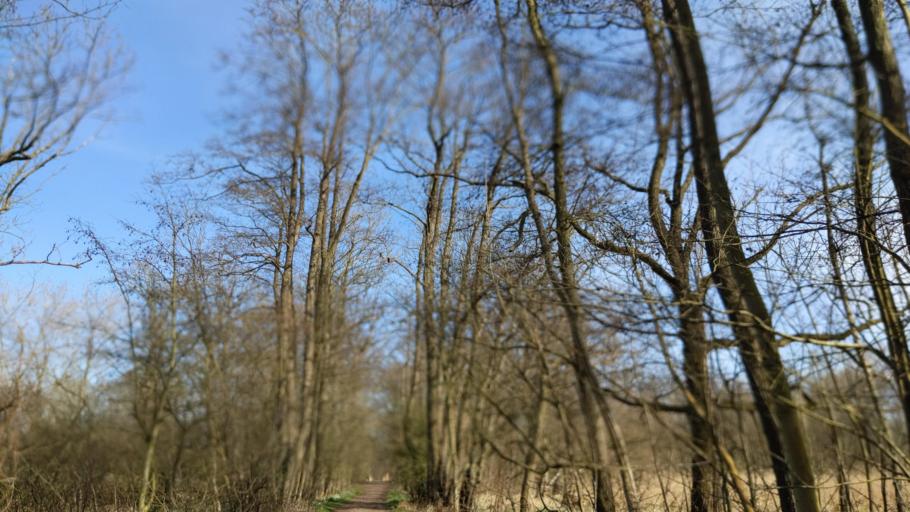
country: DE
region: Schleswig-Holstein
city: Bad Schwartau
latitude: 53.8966
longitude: 10.7163
